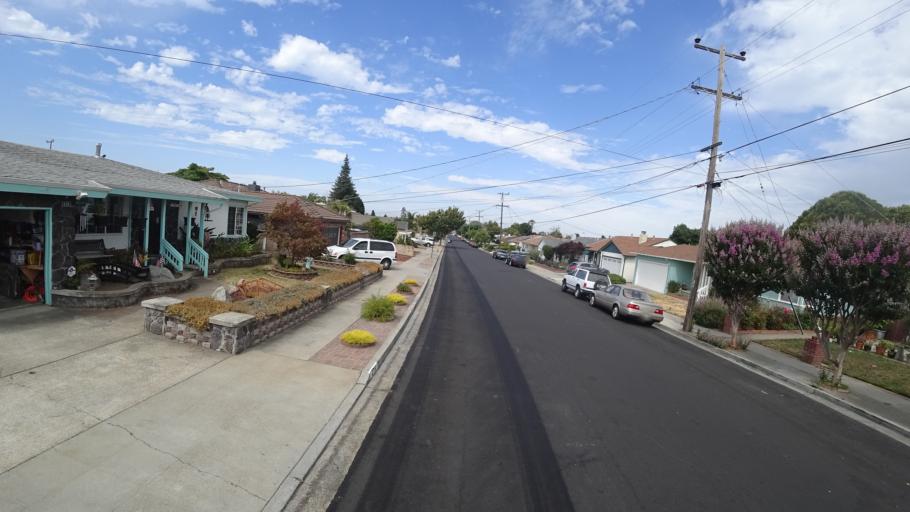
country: US
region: California
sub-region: Alameda County
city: Hayward
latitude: 37.6468
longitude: -122.0714
